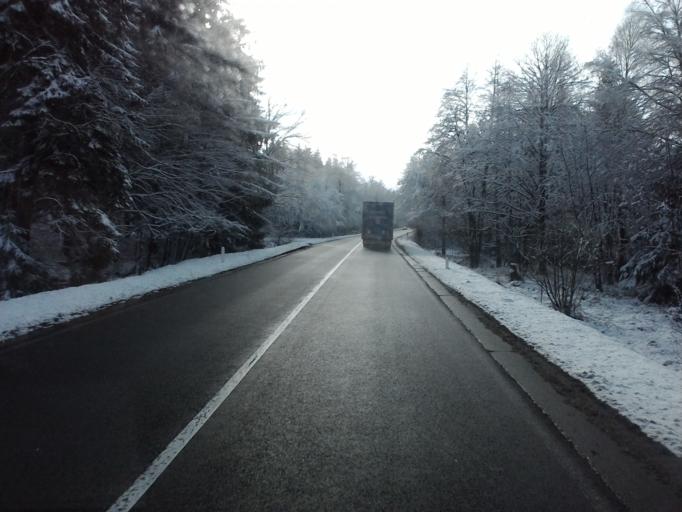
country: BE
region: Wallonia
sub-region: Province de Liege
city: Eupen
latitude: 50.5432
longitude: 6.0577
